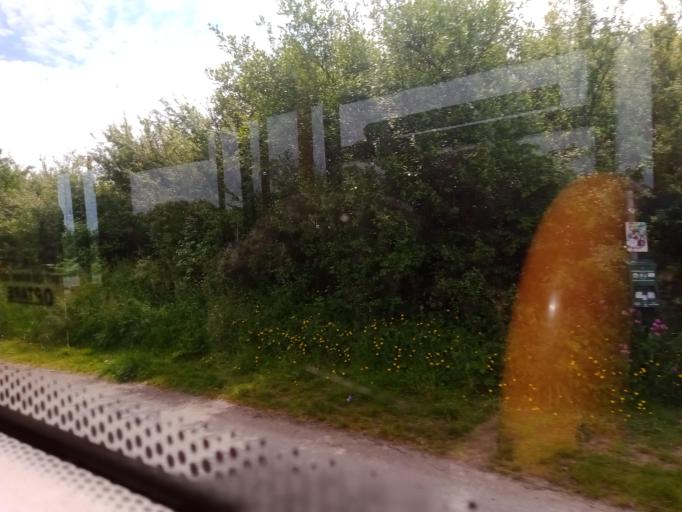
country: GB
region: Wales
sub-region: Anglesey
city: Llangoed
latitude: 53.2938
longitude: -4.1335
